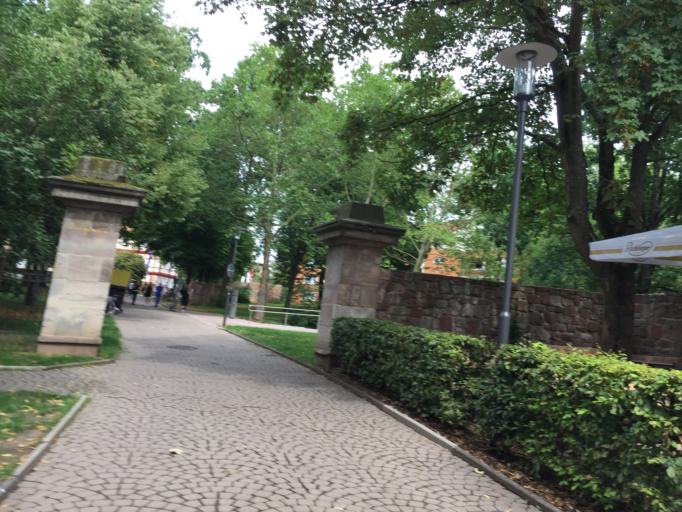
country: DE
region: Hesse
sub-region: Regierungsbezirk Kassel
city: Bad Hersfeld
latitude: 50.8662
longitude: 9.7036
